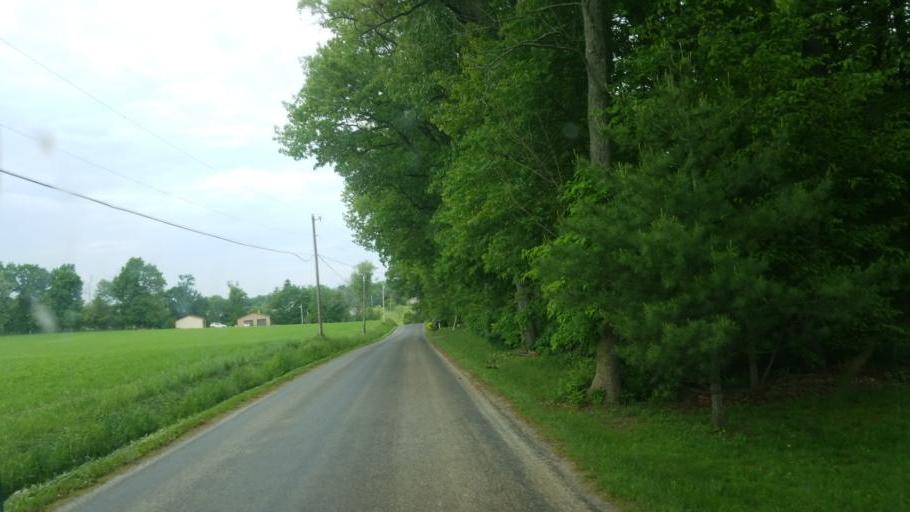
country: US
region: Ohio
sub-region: Wayne County
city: Dalton
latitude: 40.7834
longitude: -81.7362
